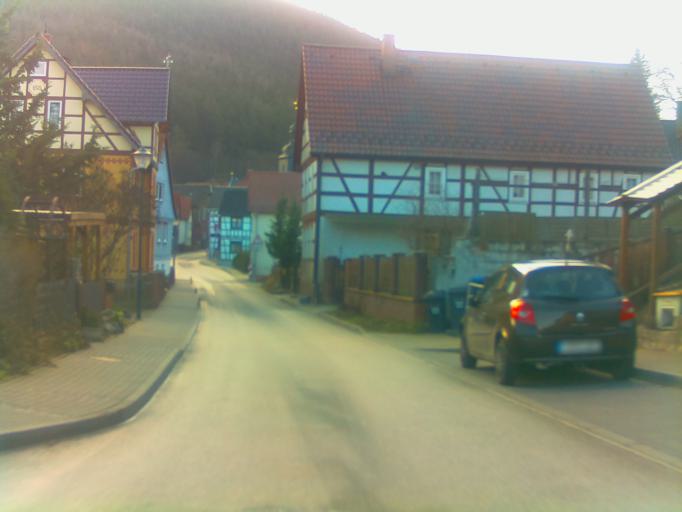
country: DE
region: Thuringia
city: Bad Blankenburg
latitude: 50.6680
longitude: 11.2914
